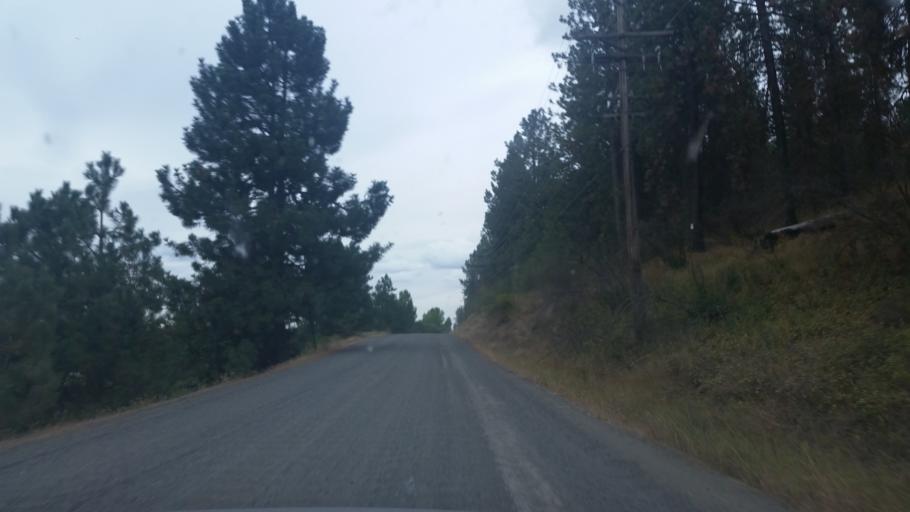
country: US
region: Washington
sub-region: Spokane County
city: Cheney
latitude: 47.5548
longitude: -117.6061
